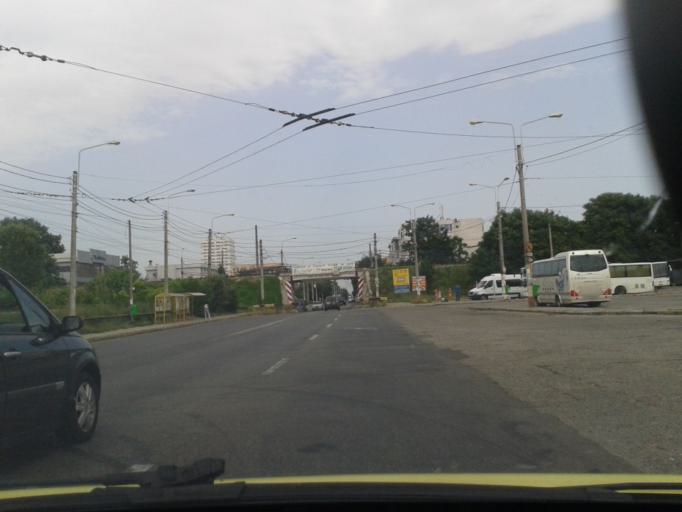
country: RO
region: Prahova
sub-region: Comuna Targsoru Vechi
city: Strejnicu
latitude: 44.9391
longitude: 25.9794
